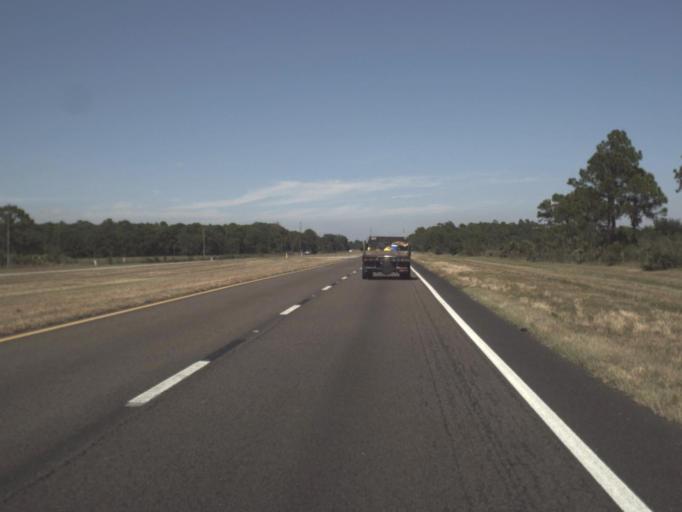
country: US
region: Florida
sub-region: Highlands County
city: Placid Lakes
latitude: 27.0938
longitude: -81.3334
